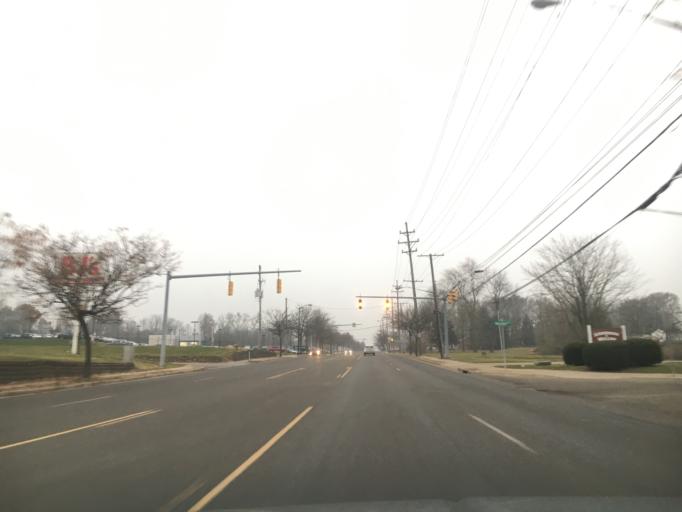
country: US
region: Ohio
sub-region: Summit County
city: Cuyahoga Falls
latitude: 41.1166
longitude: -81.4852
